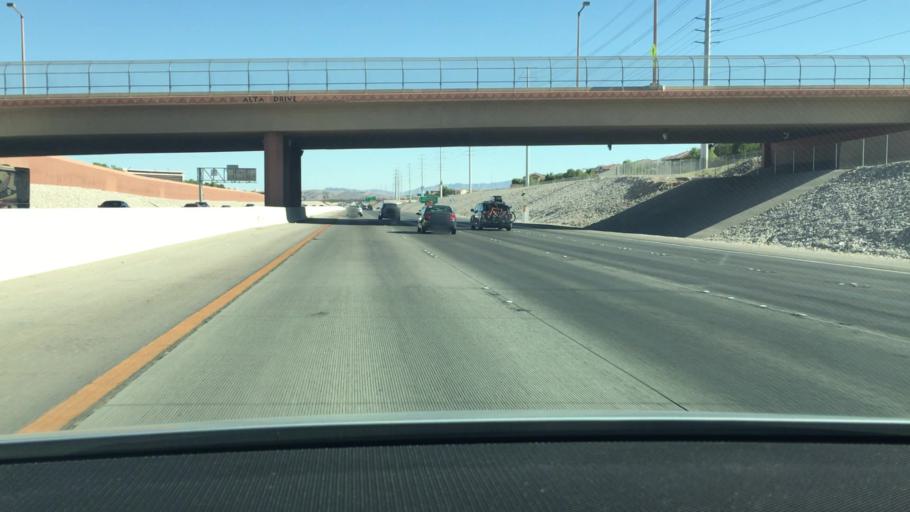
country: US
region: Nevada
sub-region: Clark County
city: Summerlin South
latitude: 36.1706
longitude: -115.3378
